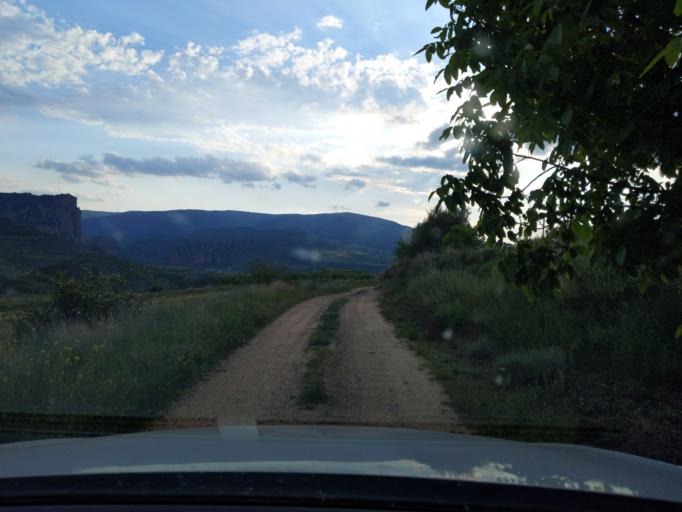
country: ES
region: La Rioja
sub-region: Provincia de La Rioja
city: Nalda
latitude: 42.3279
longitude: -2.4767
